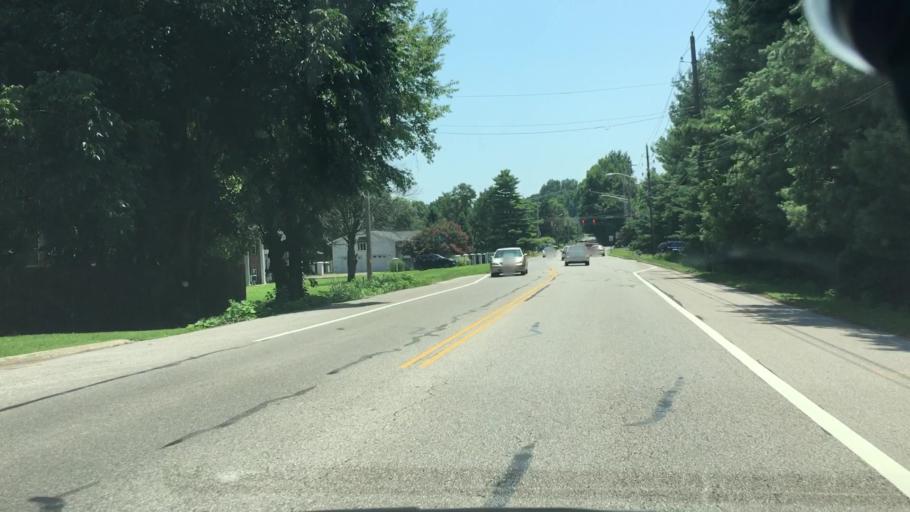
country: US
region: Indiana
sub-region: Vanderburgh County
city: Melody Hill
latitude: 37.9711
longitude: -87.4744
